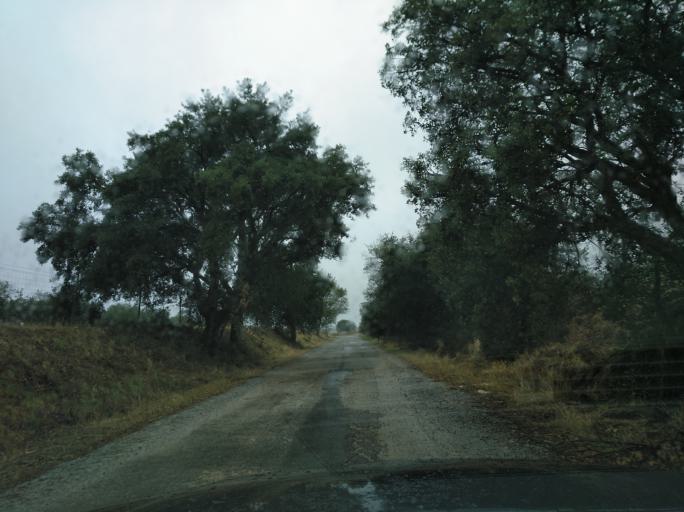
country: PT
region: Portalegre
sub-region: Campo Maior
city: Campo Maior
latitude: 38.9752
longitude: -7.0791
